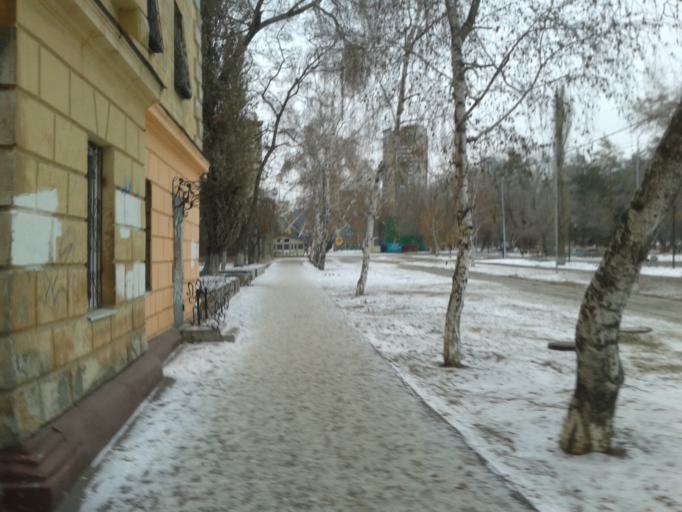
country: RU
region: Volgograd
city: Volgograd
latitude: 48.7076
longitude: 44.5099
